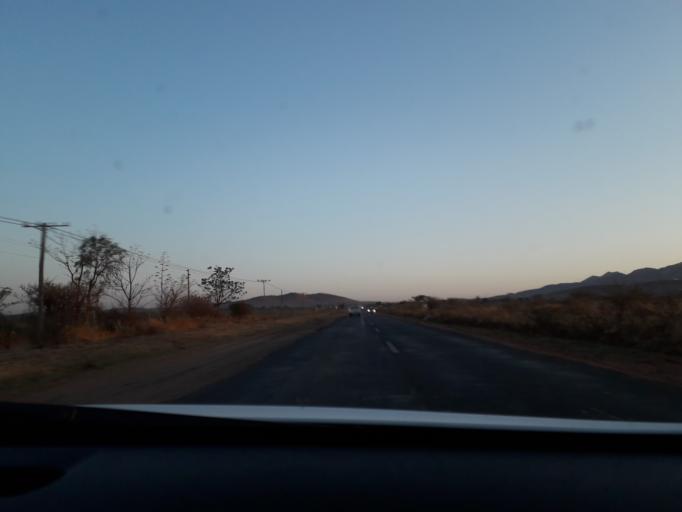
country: ZA
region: Limpopo
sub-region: Waterberg District Municipality
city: Mokopane
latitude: -24.0934
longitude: 28.9690
